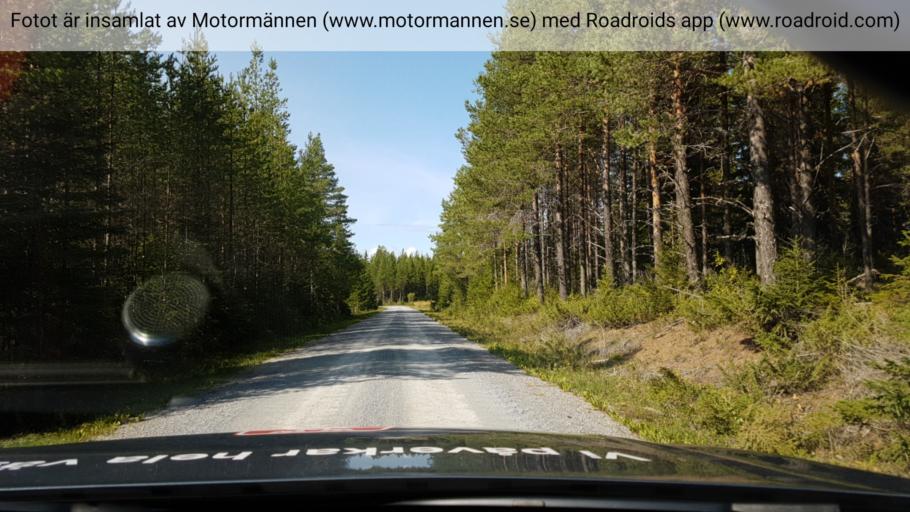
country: SE
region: Jaemtland
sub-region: OEstersunds Kommun
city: Ostersund
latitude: 63.1135
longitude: 14.5216
